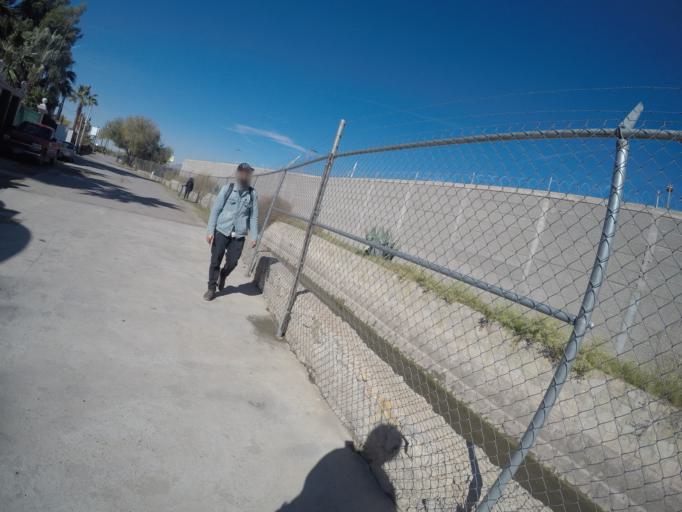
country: MX
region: Chihuahua
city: Ciudad Juarez
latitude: 31.7282
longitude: -106.4217
